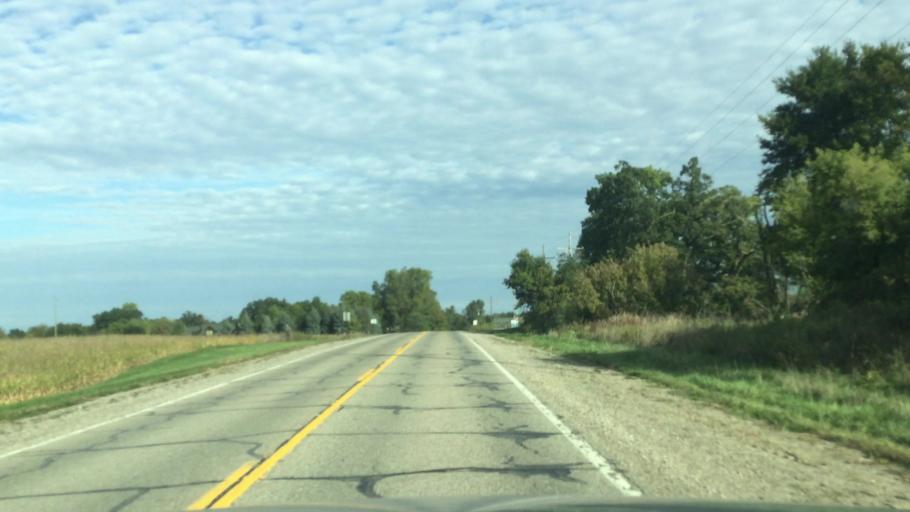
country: US
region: Michigan
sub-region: Livingston County
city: Howell
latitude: 42.5544
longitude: -83.8846
